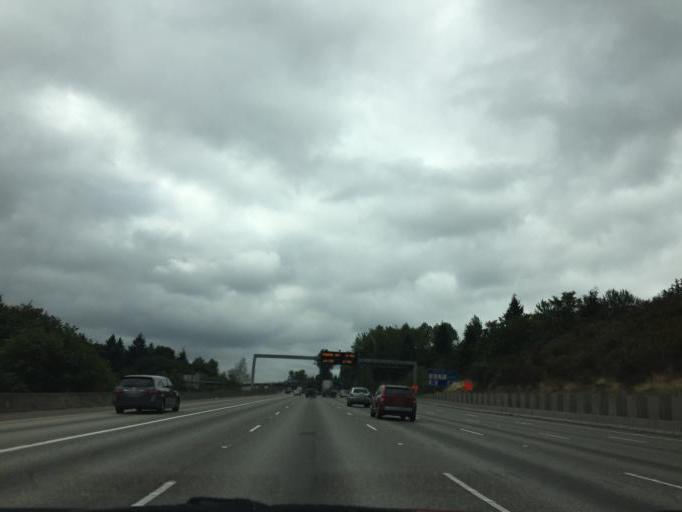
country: US
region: Washington
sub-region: King County
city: Tukwila
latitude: 47.4494
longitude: -122.2664
